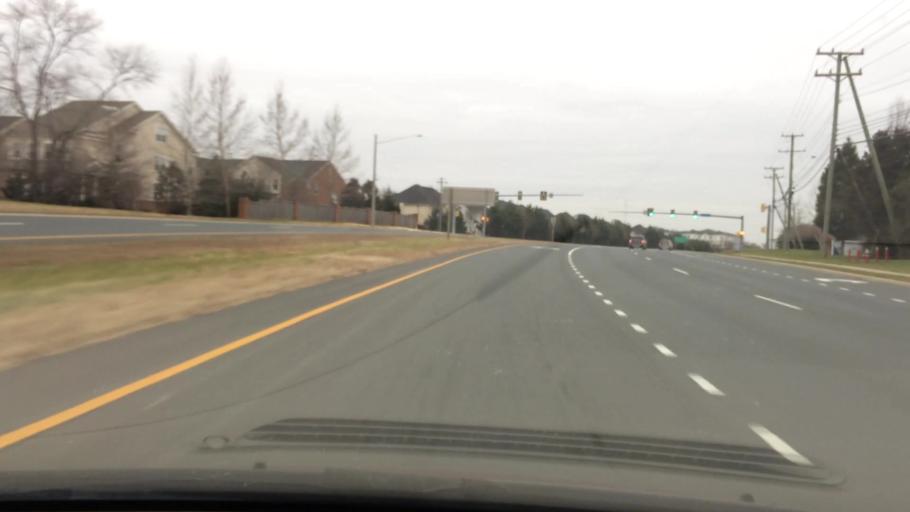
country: US
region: Virginia
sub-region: Fairfax County
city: Chantilly
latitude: 38.9029
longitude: -77.4243
